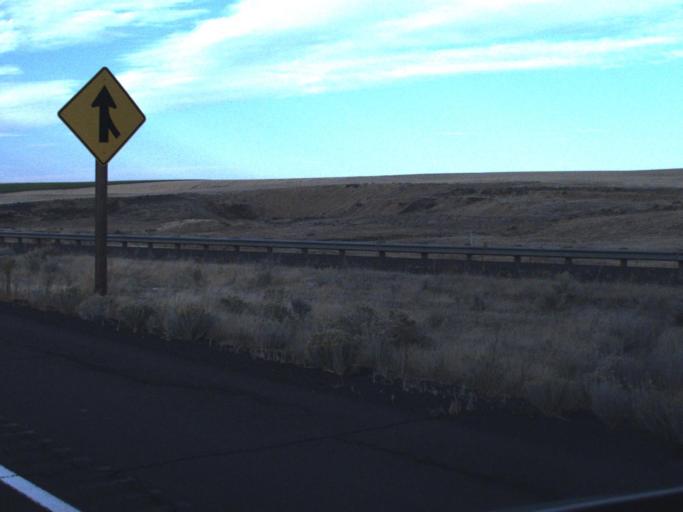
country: US
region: Washington
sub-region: Franklin County
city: Connell
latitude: 46.7882
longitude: -118.7545
